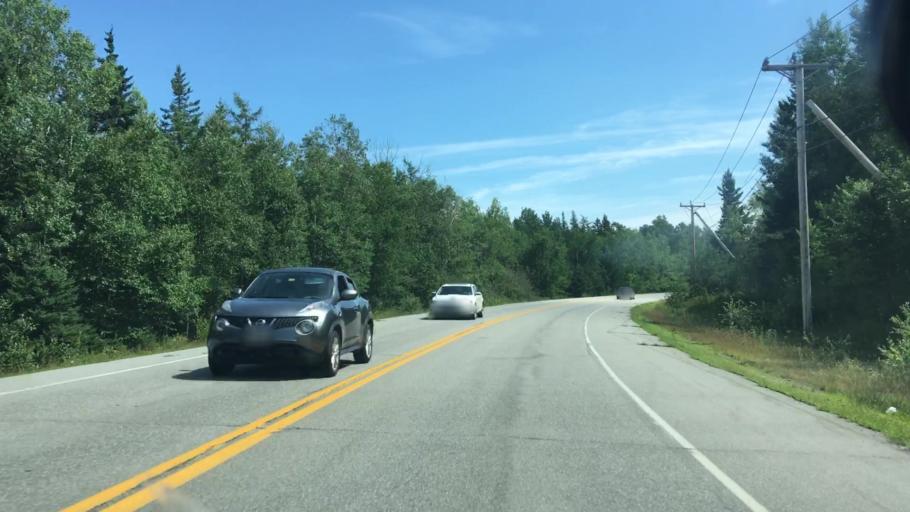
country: US
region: Maine
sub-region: Washington County
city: Eastport
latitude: 44.9375
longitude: -67.0280
